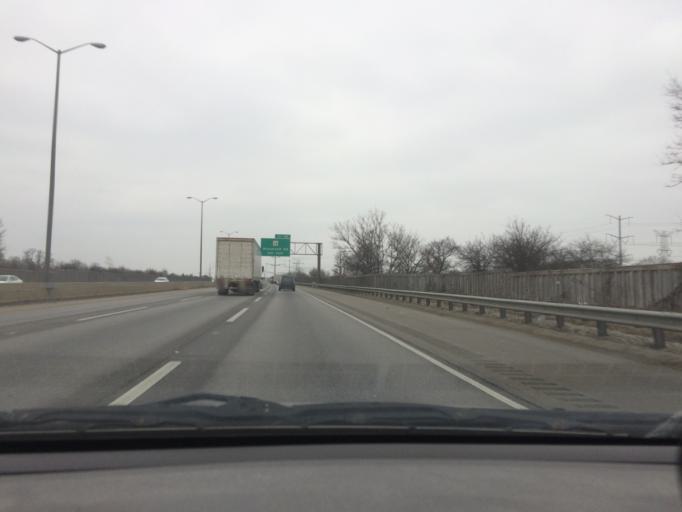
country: US
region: Illinois
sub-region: DuPage County
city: Glen Ellyn
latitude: 41.8697
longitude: -88.0378
